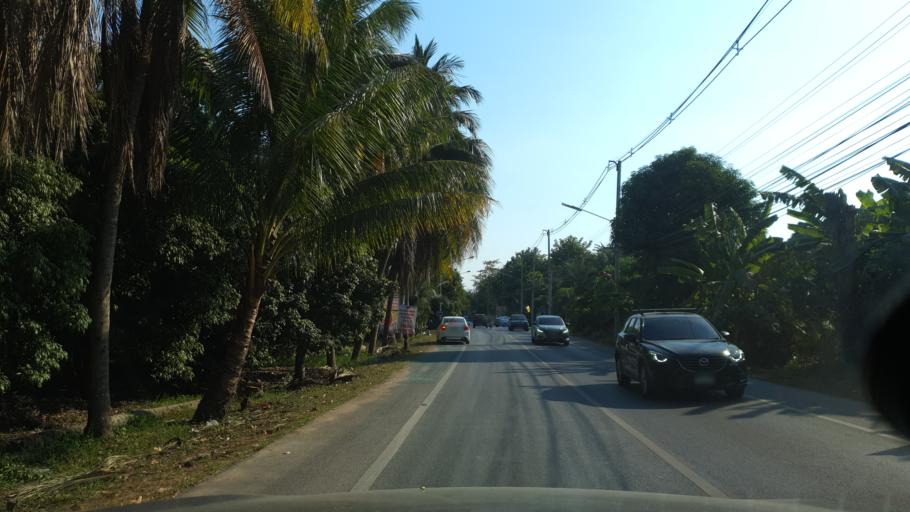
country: TH
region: Samut Songkhram
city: Amphawa
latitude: 13.4439
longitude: 99.9413
